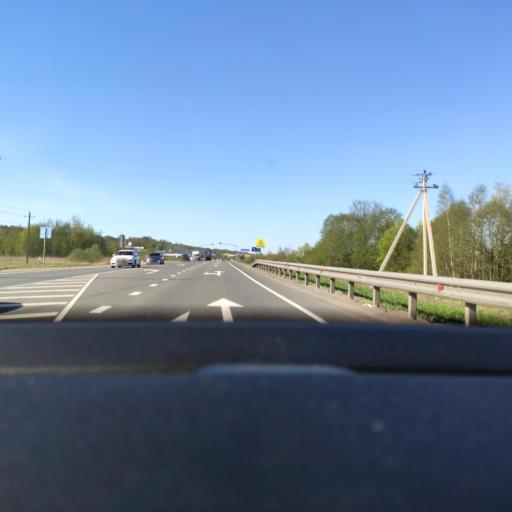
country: RU
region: Moskovskaya
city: Yakhroma
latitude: 56.3062
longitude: 37.4796
